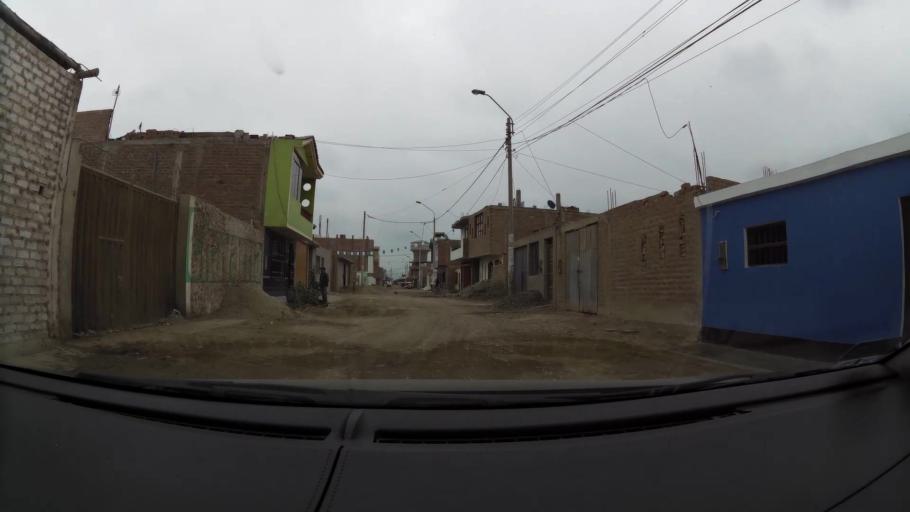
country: PE
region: Lima
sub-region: Provincia de Huaral
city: Huaral
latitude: -11.5020
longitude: -77.2319
